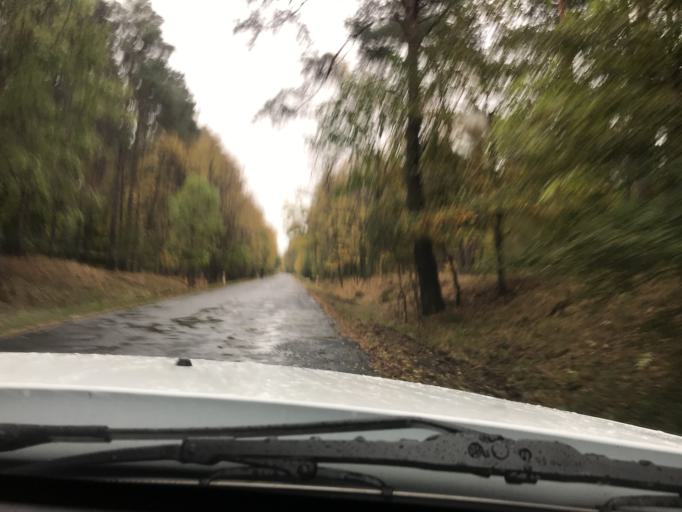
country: PL
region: West Pomeranian Voivodeship
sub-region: Powiat gryfinski
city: Moryn
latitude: 52.7826
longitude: 14.4141
